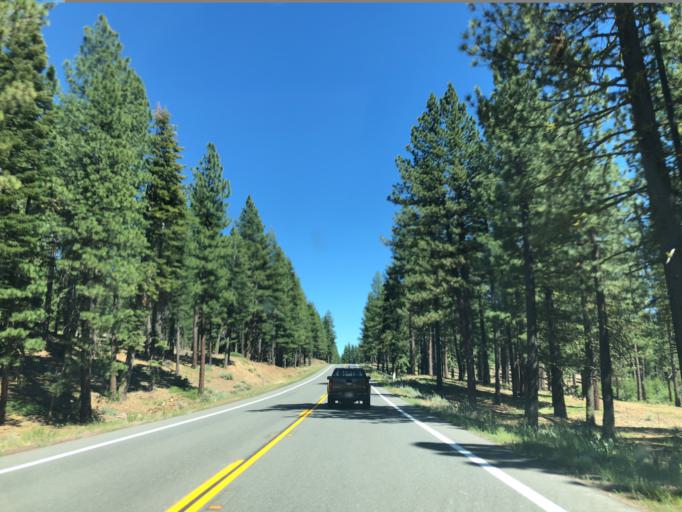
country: US
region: California
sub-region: Lassen County
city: Westwood
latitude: 40.4410
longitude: -120.8602
